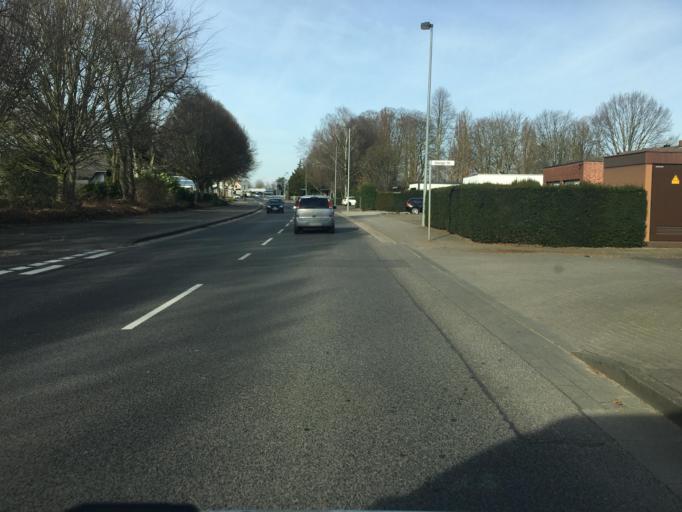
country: DE
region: North Rhine-Westphalia
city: Erkelenz
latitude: 51.0844
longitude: 6.3116
